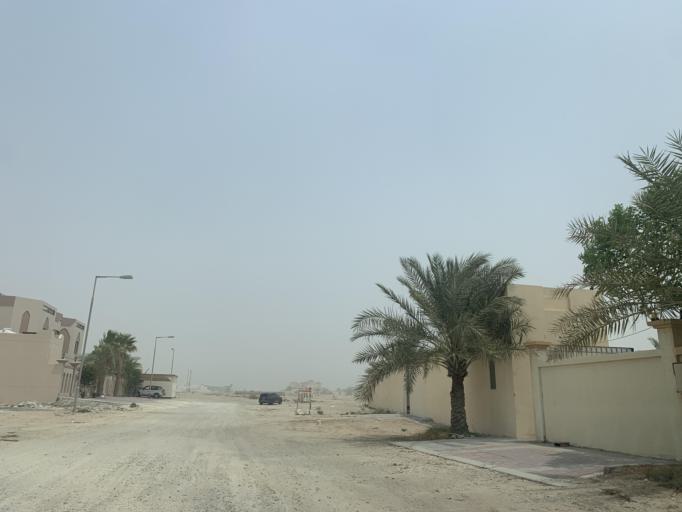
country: BH
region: Central Governorate
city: Madinat Hamad
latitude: 26.1713
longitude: 50.4734
